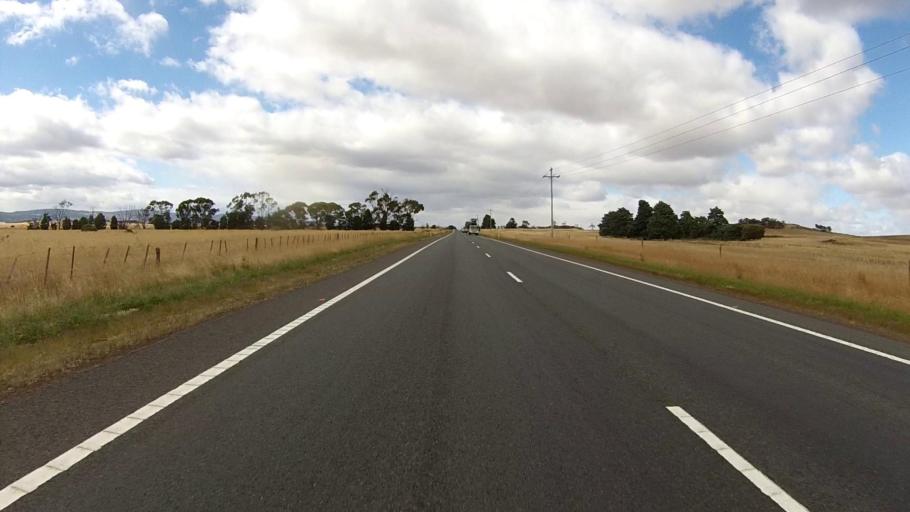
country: AU
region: Tasmania
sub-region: Northern Midlands
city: Evandale
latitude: -41.8933
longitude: 147.4720
